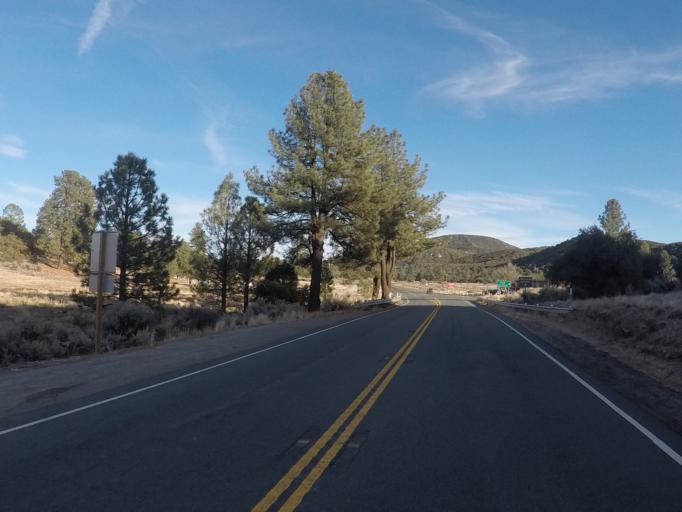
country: US
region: California
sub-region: Riverside County
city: Anza
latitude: 33.5706
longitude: -116.5927
